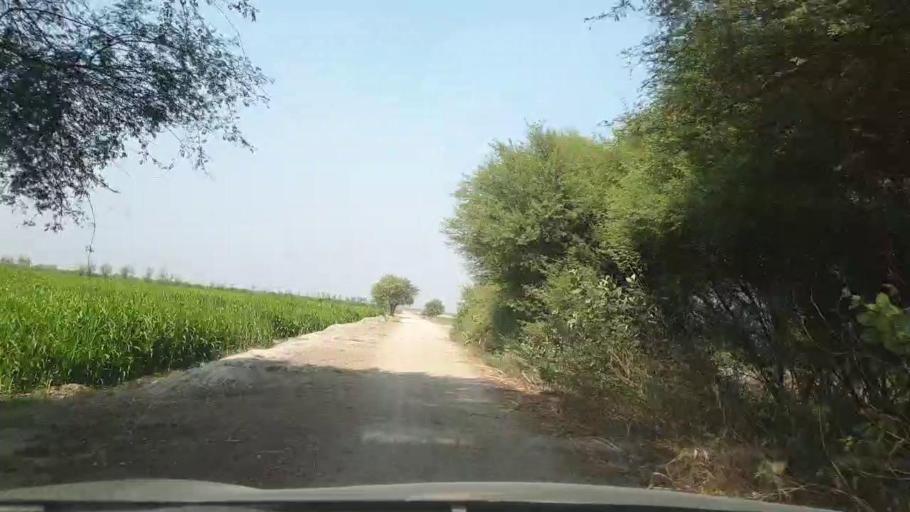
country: PK
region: Sindh
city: Tando Allahyar
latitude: 25.5654
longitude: 68.8256
